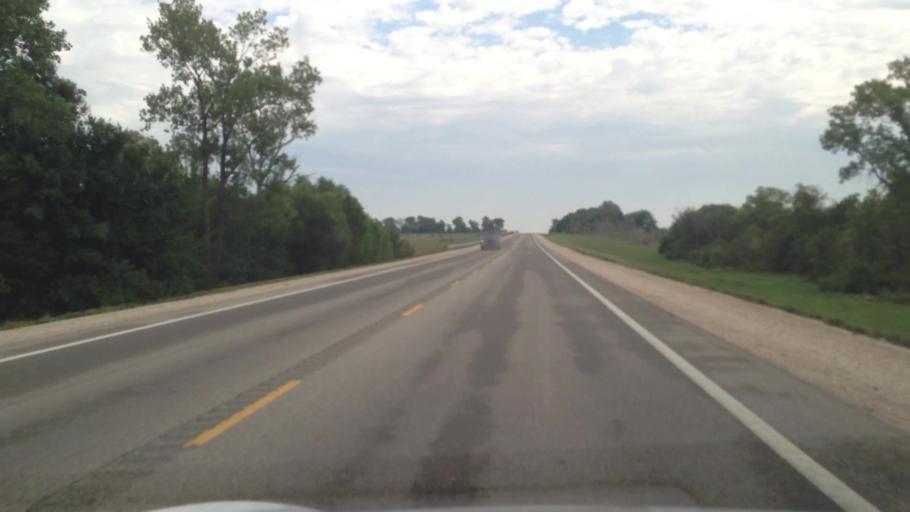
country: US
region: Kansas
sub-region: Allen County
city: Iola
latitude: 37.9095
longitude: -95.1149
